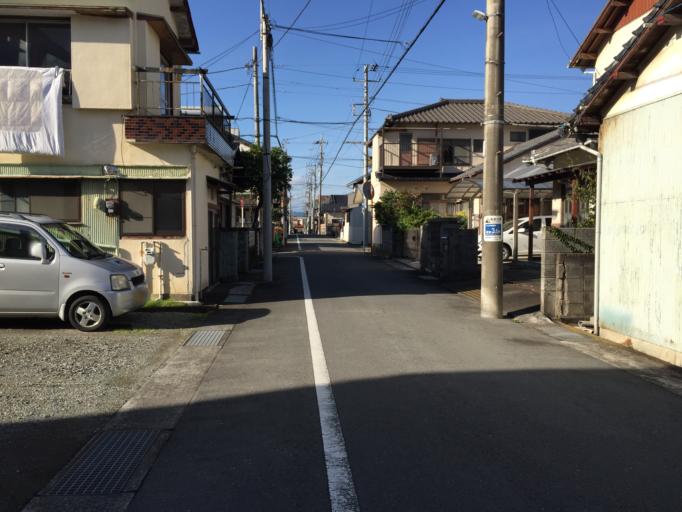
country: JP
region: Shizuoka
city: Numazu
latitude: 35.0766
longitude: 138.8608
